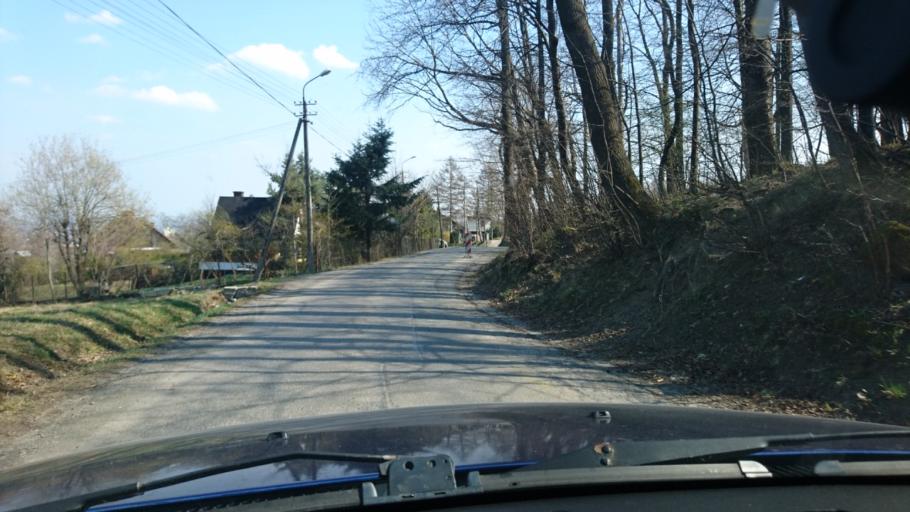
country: PL
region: Silesian Voivodeship
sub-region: Powiat bielski
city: Kozy
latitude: 49.8191
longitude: 19.1152
